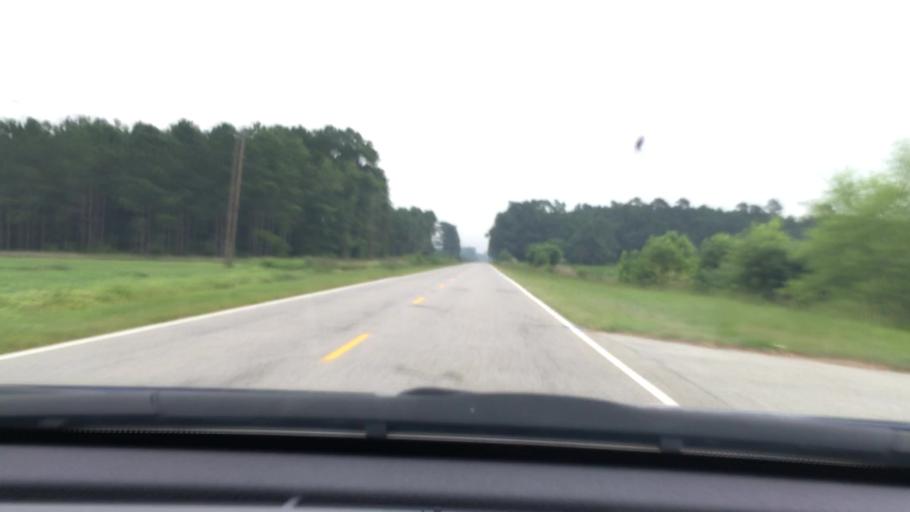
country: US
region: South Carolina
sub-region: Lee County
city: Bishopville
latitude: 34.0855
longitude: -80.1904
